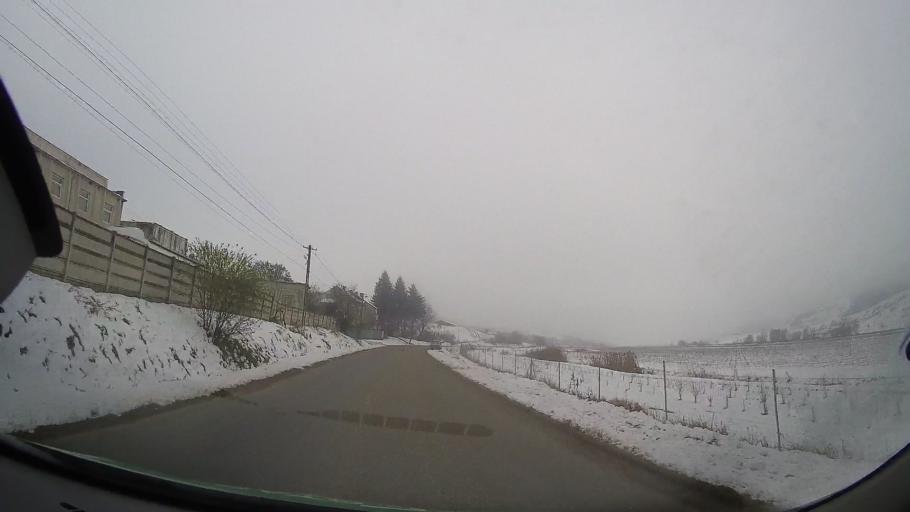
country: RO
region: Bacau
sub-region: Comuna Vultureni
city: Vultureni
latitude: 46.3669
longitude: 27.2845
